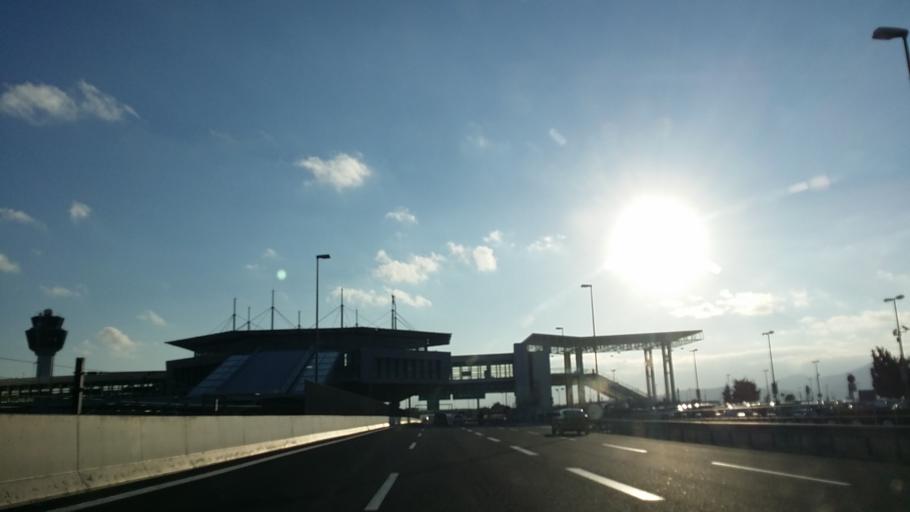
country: GR
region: Attica
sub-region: Nomarchia Anatolikis Attikis
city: Spata
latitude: 37.9382
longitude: 23.9456
